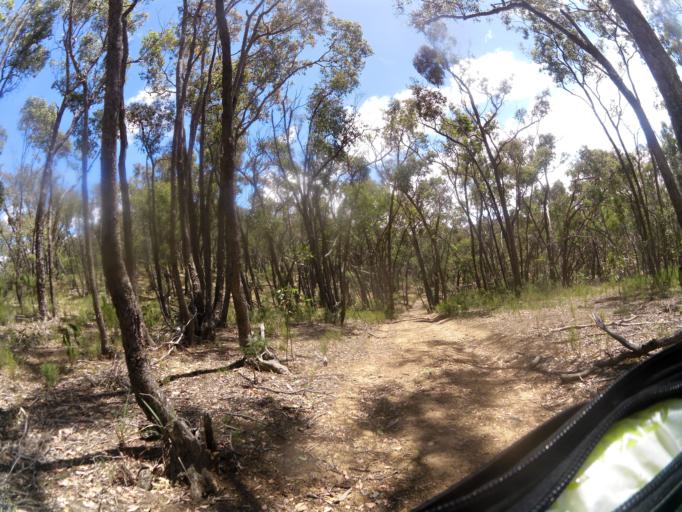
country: AU
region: Victoria
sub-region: Mount Alexander
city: Castlemaine
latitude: -37.0643
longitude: 144.2662
